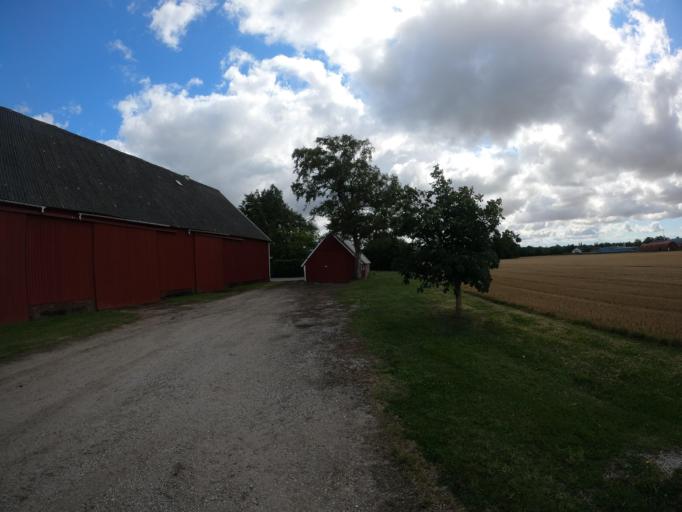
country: SE
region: Skane
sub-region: Eslovs Kommun
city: Eslov
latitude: 55.7283
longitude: 13.3480
